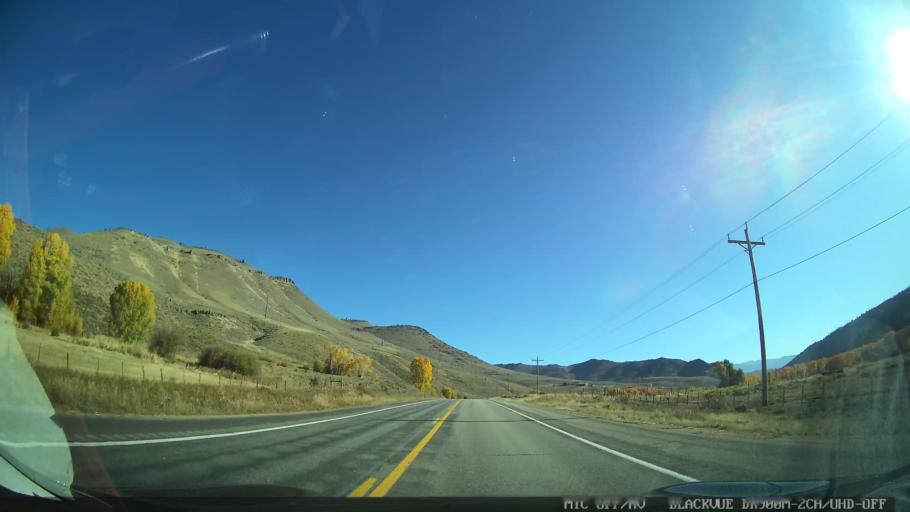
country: US
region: Colorado
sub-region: Grand County
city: Hot Sulphur Springs
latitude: 40.1042
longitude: -106.0266
